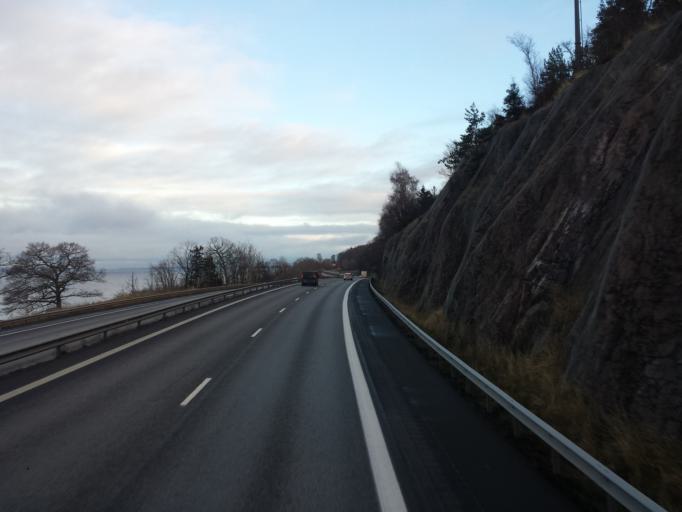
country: SE
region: Joenkoeping
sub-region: Jonkopings Kommun
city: Kaxholmen
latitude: 57.8696
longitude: 14.2718
